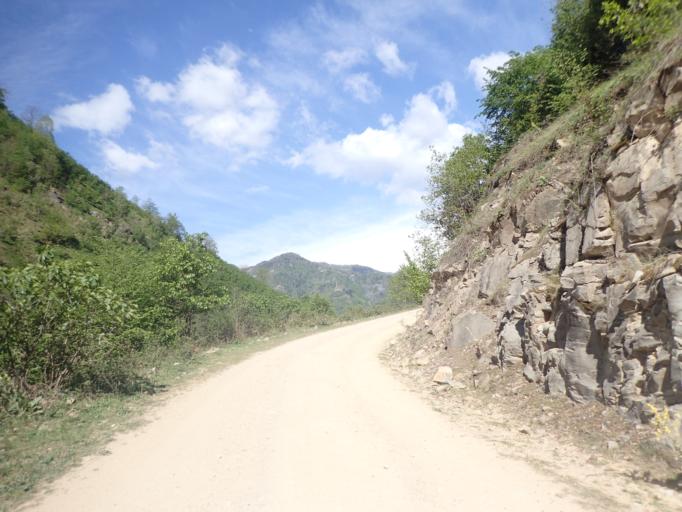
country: TR
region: Ordu
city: Topcam
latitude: 40.7090
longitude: 37.8829
